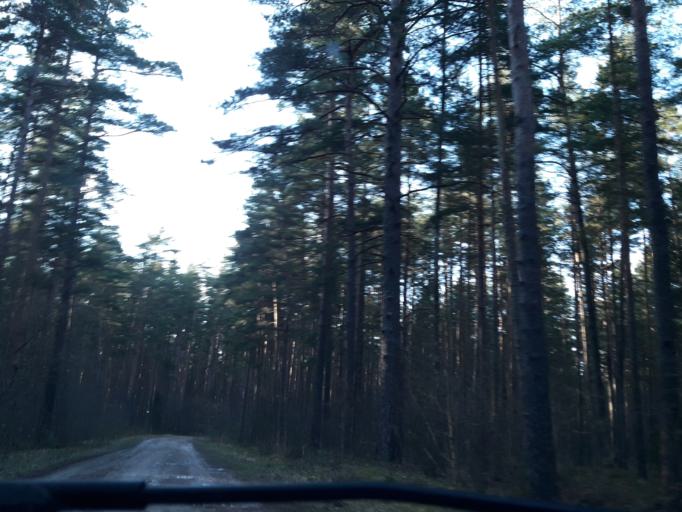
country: LV
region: Kekava
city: Kekava
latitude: 56.8648
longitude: 24.2225
